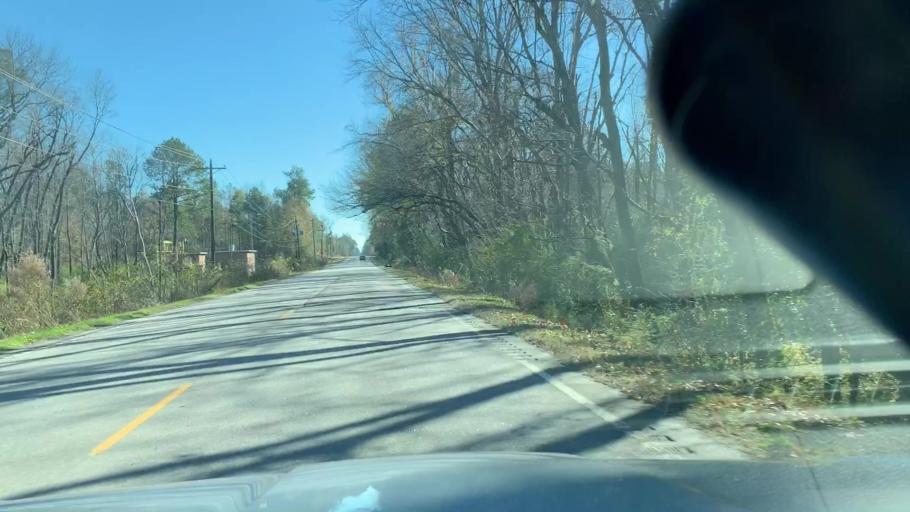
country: US
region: South Carolina
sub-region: Richland County
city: Hopkins
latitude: 33.9237
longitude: -80.9583
